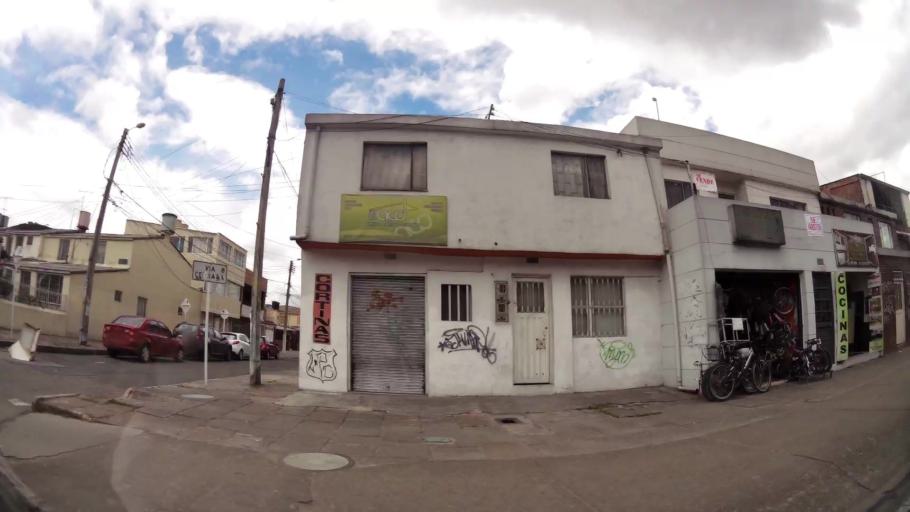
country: CO
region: Bogota D.C.
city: Bogota
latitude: 4.6916
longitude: -74.1081
